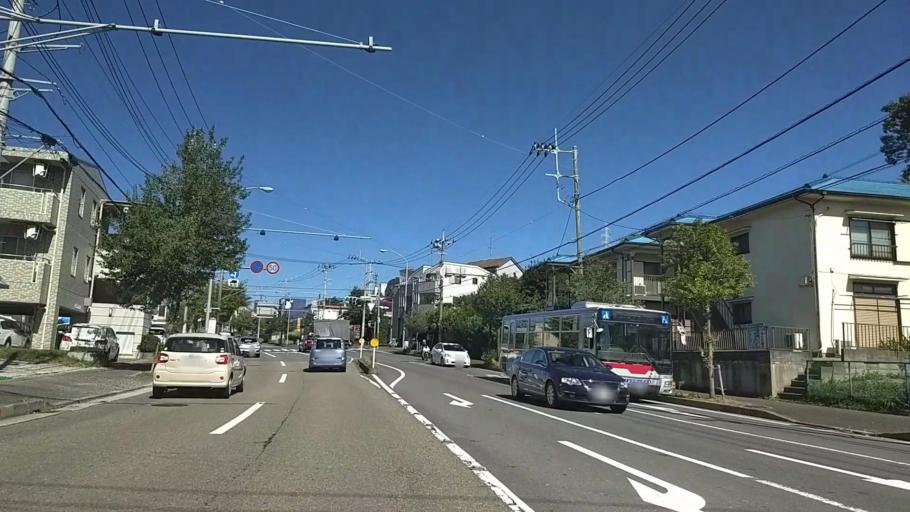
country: JP
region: Tokyo
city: Chofugaoka
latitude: 35.5869
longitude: 139.5428
